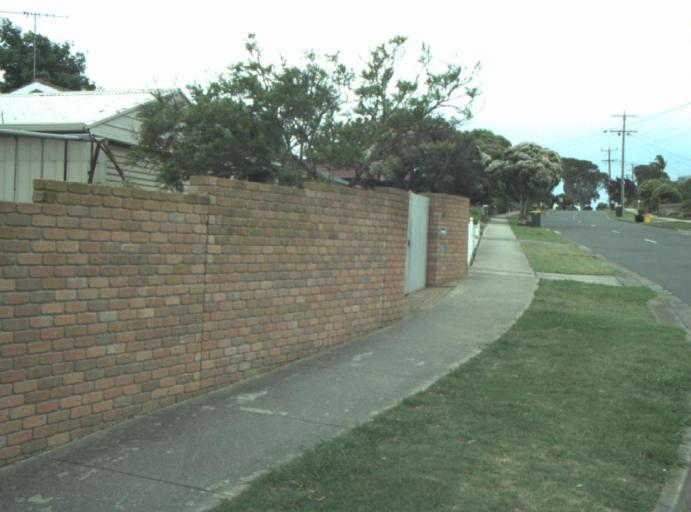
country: AU
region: Victoria
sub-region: Greater Geelong
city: Leopold
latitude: -38.1825
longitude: 144.4711
